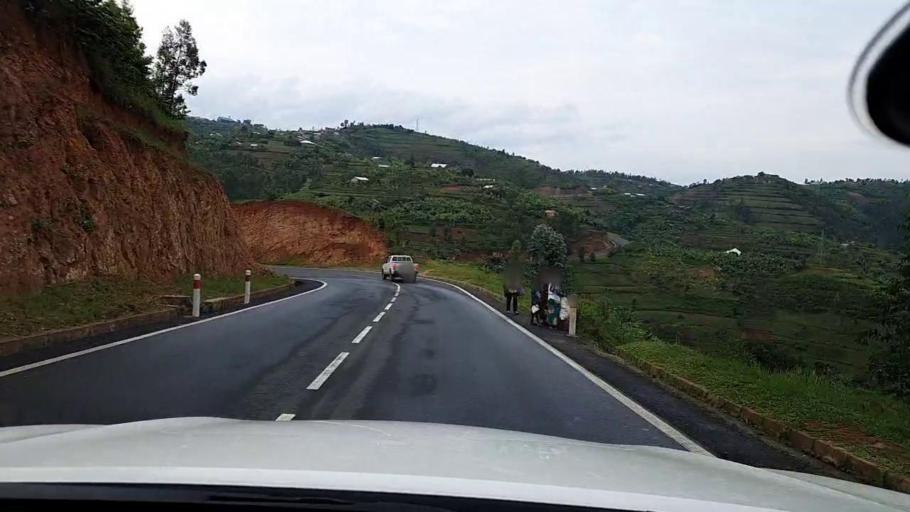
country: RW
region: Western Province
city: Kibuye
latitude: -2.1626
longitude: 29.2956
